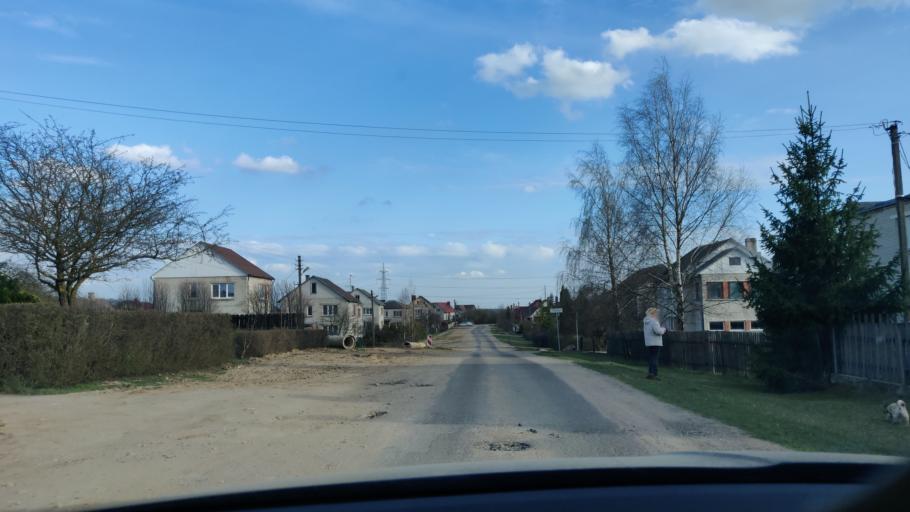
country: LT
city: Trakai
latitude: 54.6081
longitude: 24.9755
